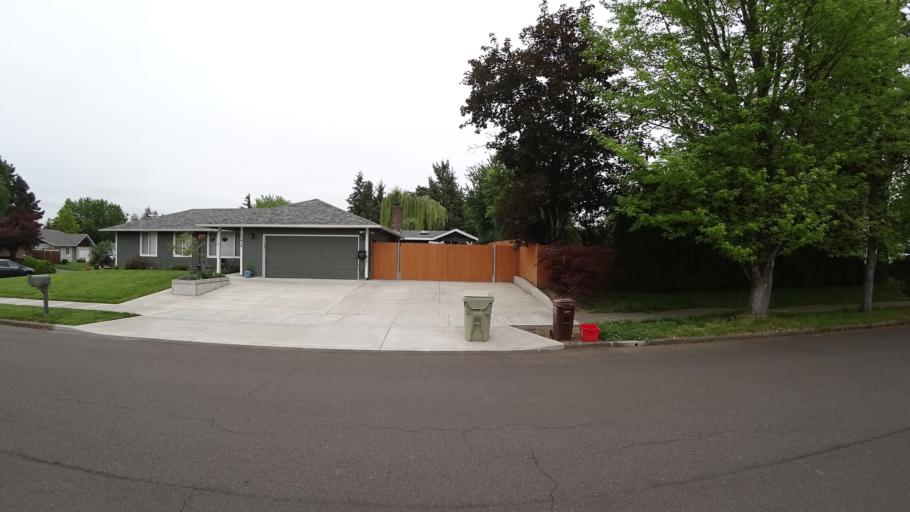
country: US
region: Oregon
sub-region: Washington County
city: Bethany
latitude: 45.5411
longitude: -122.8607
